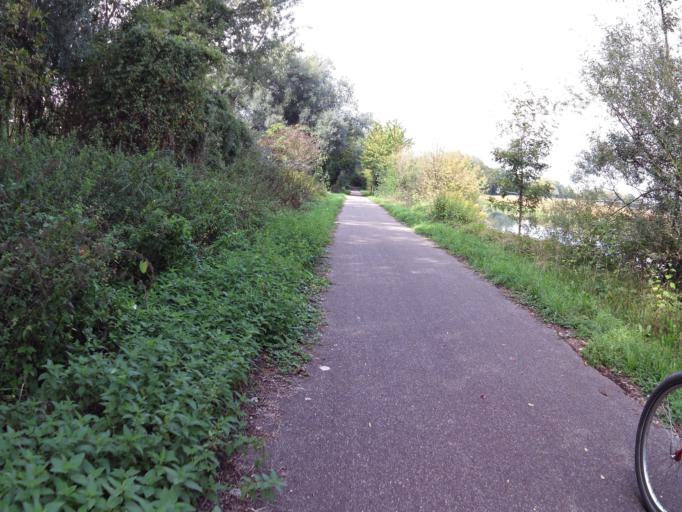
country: FR
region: Alsace
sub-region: Departement du Haut-Rhin
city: Kunheim
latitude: 48.0651
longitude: 7.5415
